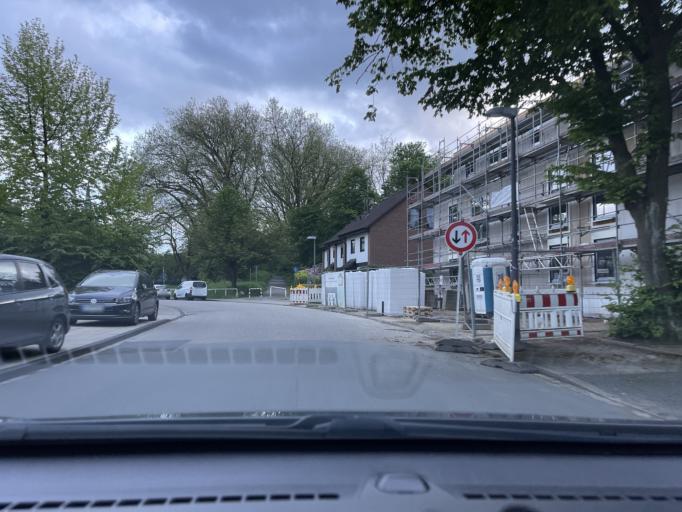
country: DE
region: North Rhine-Westphalia
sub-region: Regierungsbezirk Munster
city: Bottrop
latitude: 51.4774
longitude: 6.9468
